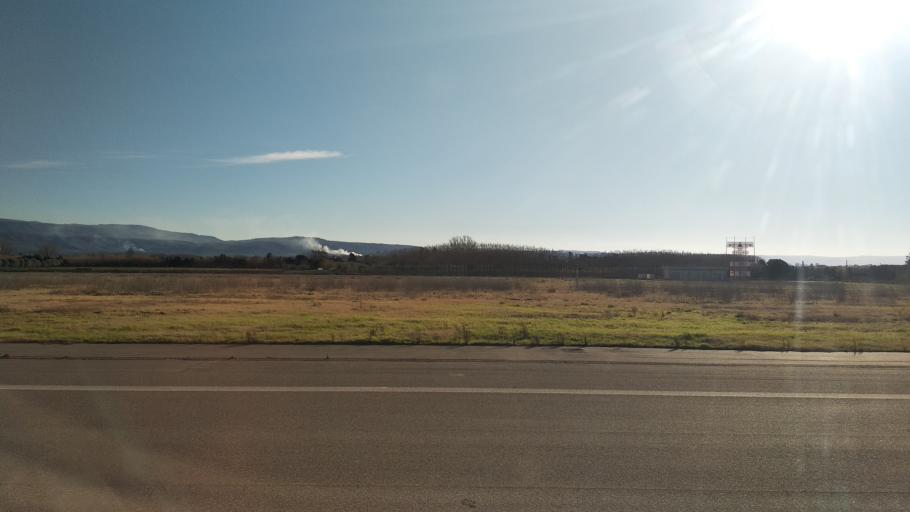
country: IT
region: Calabria
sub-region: Provincia di Catanzaro
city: Santa Eufemia Lamezia
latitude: 38.9043
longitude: 16.2524
